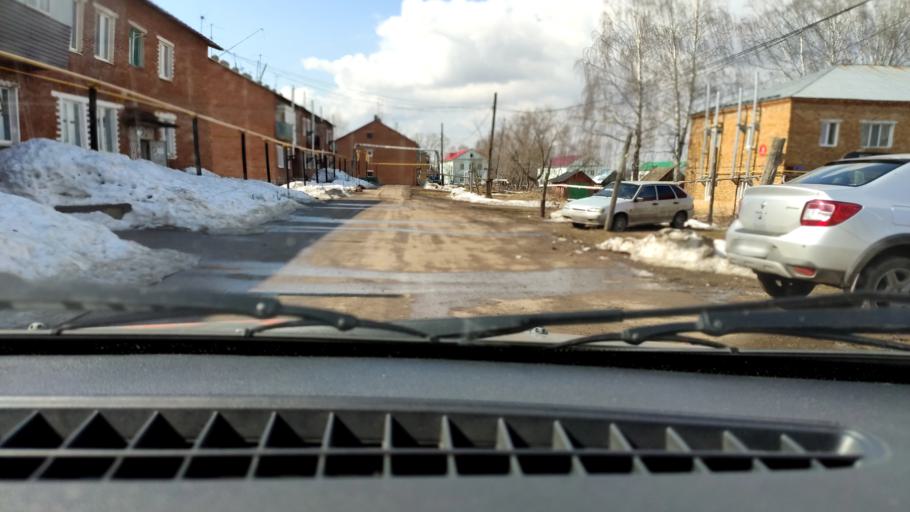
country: RU
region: Bashkortostan
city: Kudeyevskiy
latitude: 54.8679
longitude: 56.7453
